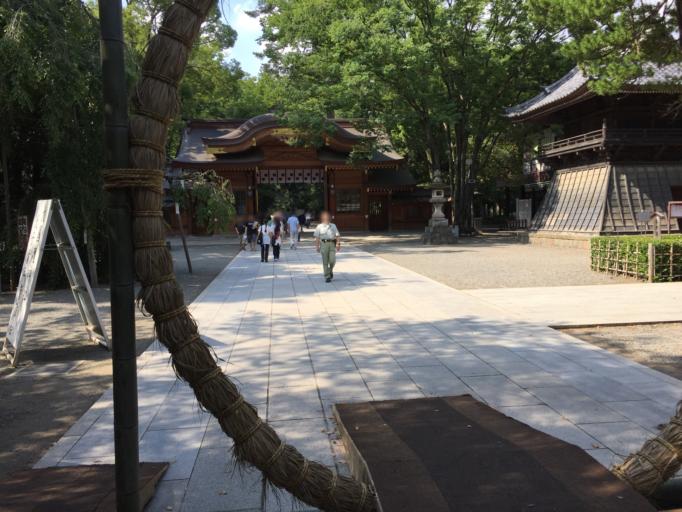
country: JP
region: Tokyo
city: Kokubunji
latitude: 35.6679
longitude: 139.4790
